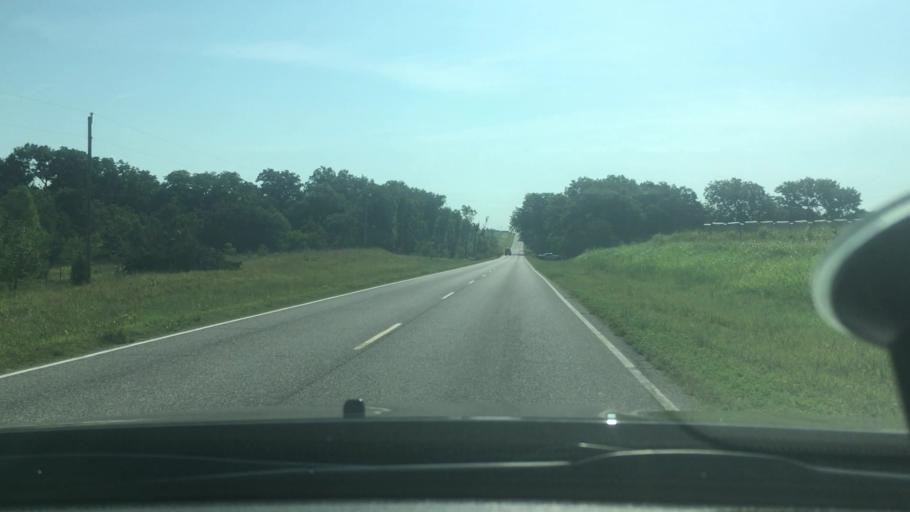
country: US
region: Oklahoma
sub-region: Garvin County
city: Pauls Valley
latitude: 34.6520
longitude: -97.3301
